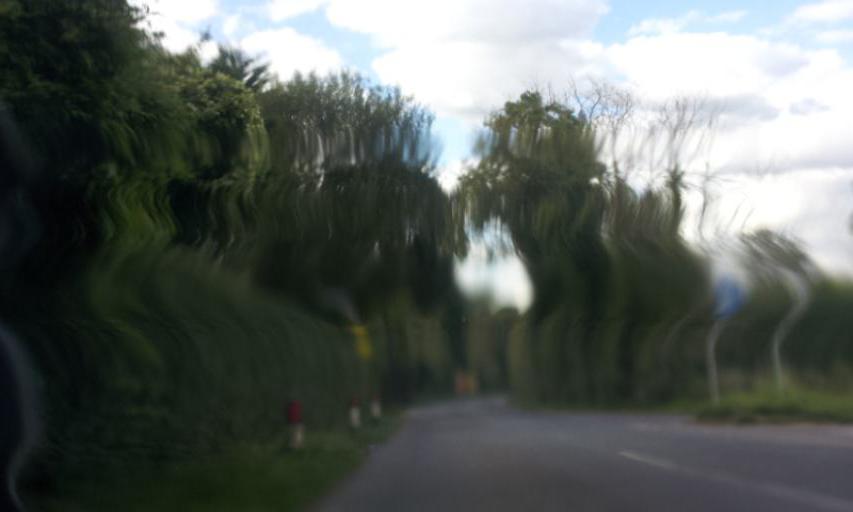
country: GB
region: England
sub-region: Kent
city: Staplehurst
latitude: 51.1806
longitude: 0.5853
